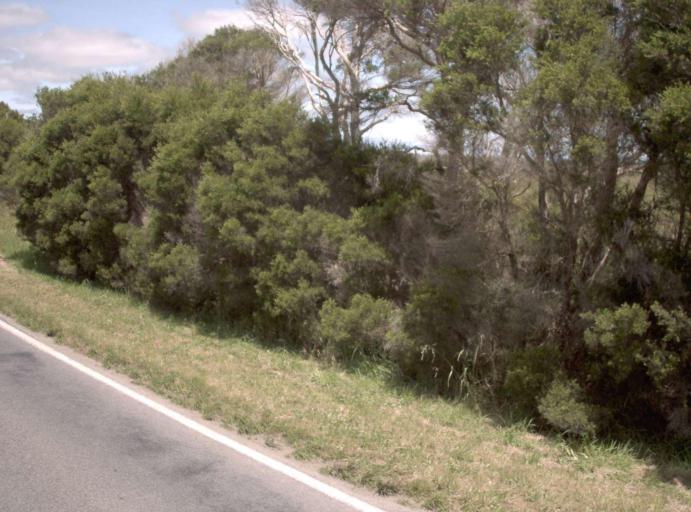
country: AU
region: Victoria
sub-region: Bass Coast
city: North Wonthaggi
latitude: -38.6399
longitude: 146.0111
